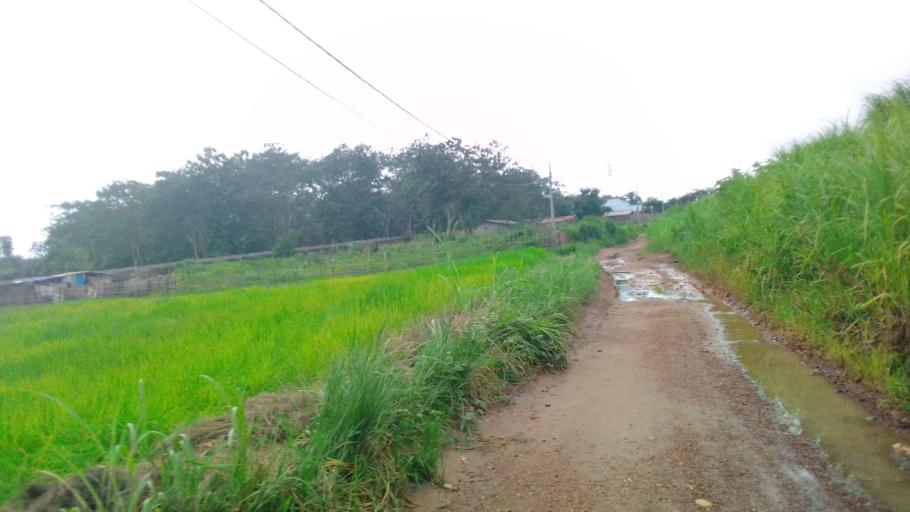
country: SL
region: Northern Province
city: Lunsar
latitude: 8.6913
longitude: -12.5480
